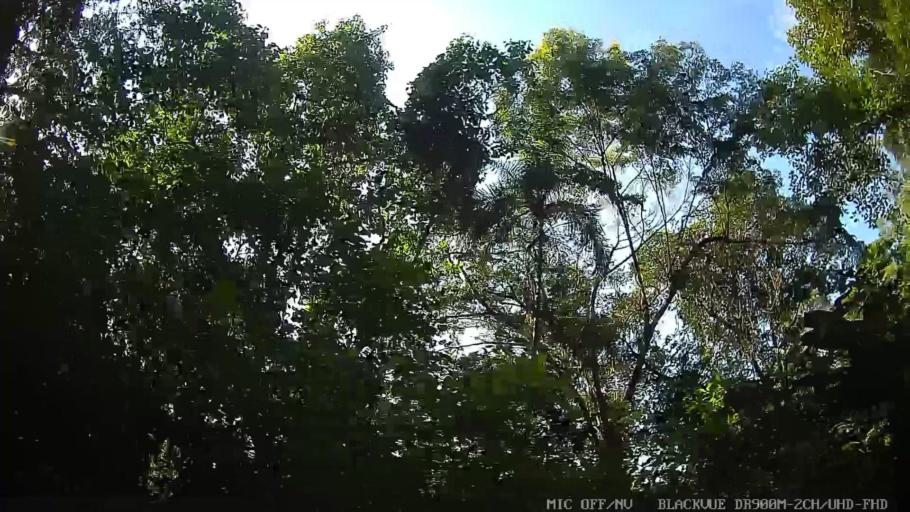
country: BR
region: Sao Paulo
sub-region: Guaruja
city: Guaruja
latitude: -23.9833
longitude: -46.2557
